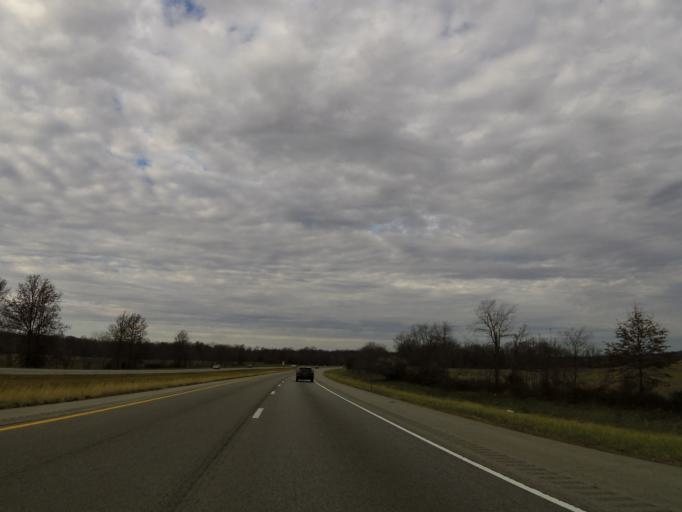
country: US
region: Illinois
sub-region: Clinton County
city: Wamac
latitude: 38.3625
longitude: -89.0773
